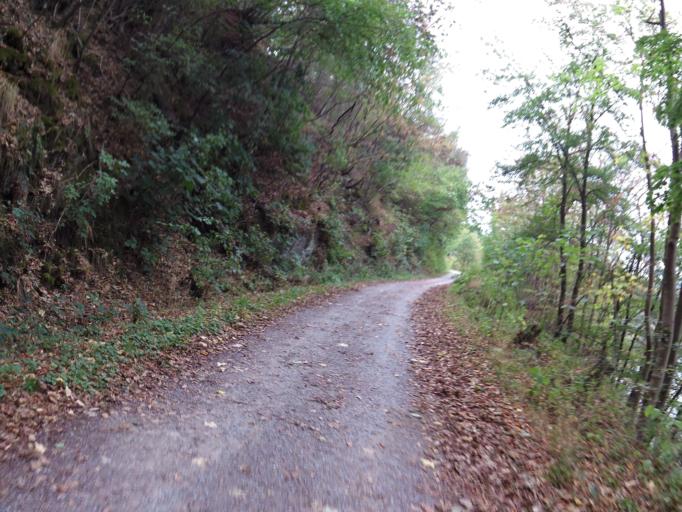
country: DE
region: North Rhine-Westphalia
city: Heimbach
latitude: 50.6347
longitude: 6.4361
